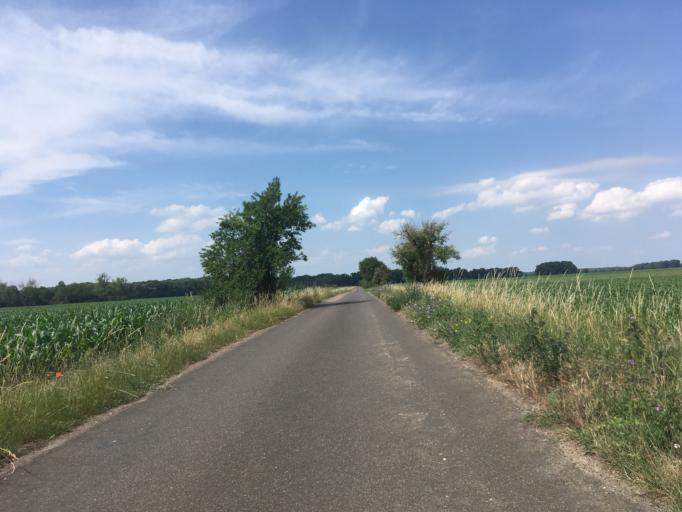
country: DE
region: Saxony-Anhalt
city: Osternienburg
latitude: 51.7593
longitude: 12.0550
